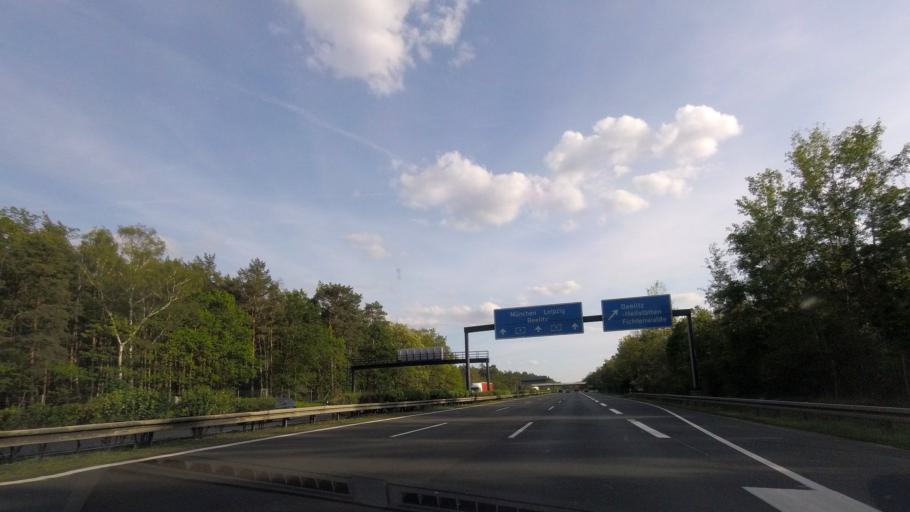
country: DE
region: Brandenburg
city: Fichtenwalde
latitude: 52.2729
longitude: 12.9104
